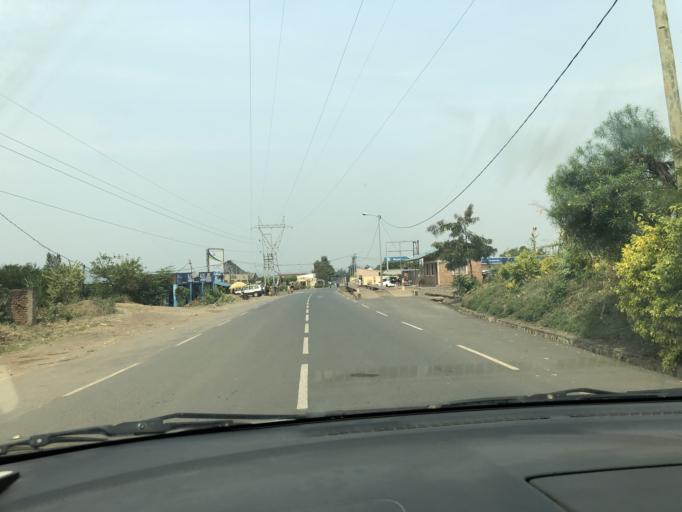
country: BI
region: Cibitoke
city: Cibitoke
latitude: -2.6988
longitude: 29.0053
